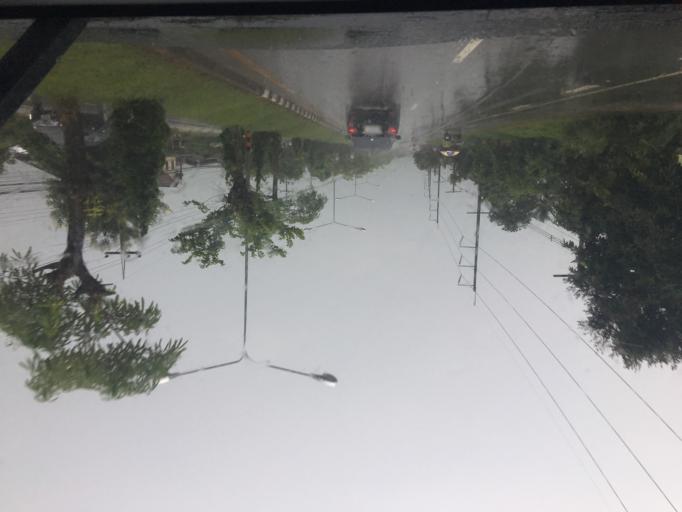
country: TH
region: Chiang Rai
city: Mae Fa Luang
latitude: 20.2574
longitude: 99.8561
